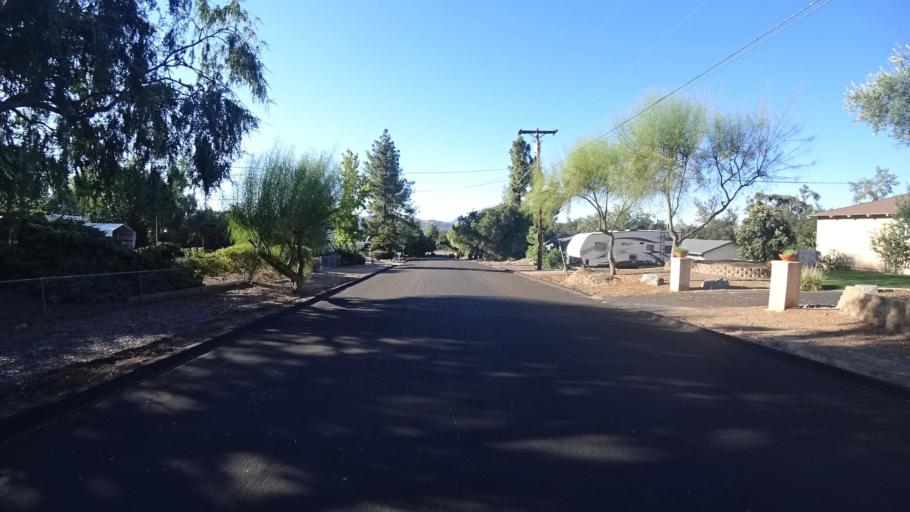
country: US
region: California
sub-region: San Diego County
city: Alpine
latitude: 32.8265
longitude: -116.7531
